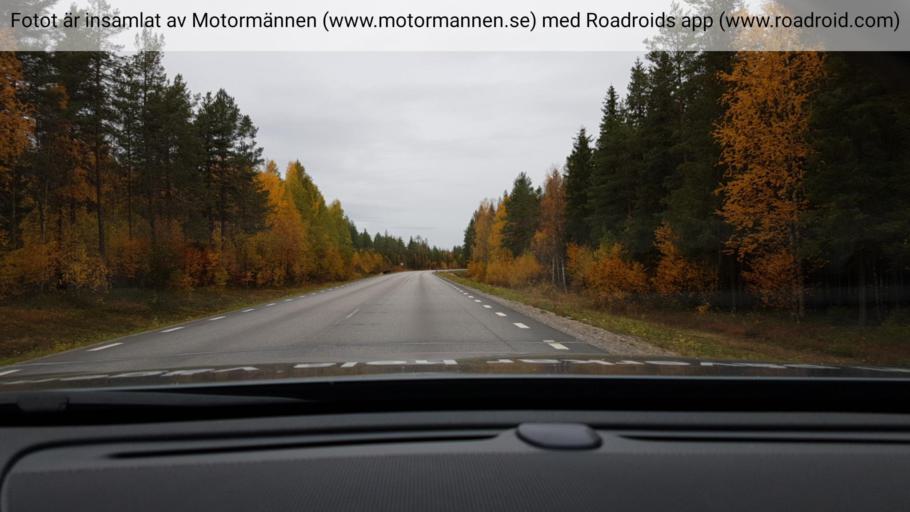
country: SE
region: Norrbotten
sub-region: Overkalix Kommun
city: OEverkalix
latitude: 66.3480
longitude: 22.8278
